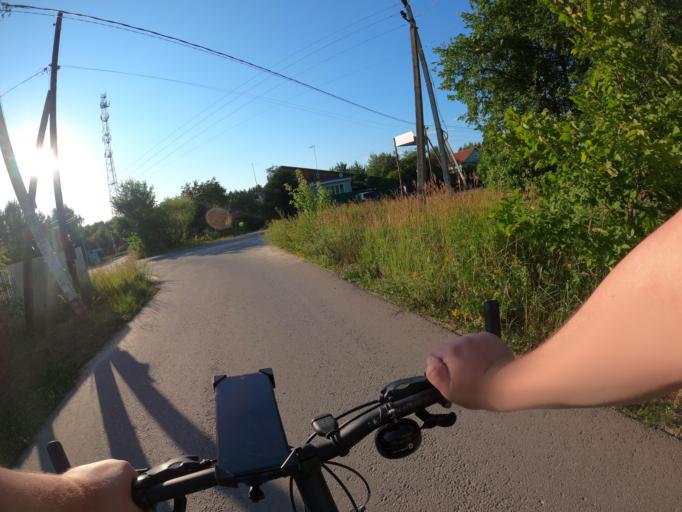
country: RU
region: Moskovskaya
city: Beloozerskiy
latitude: 55.4902
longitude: 38.4325
